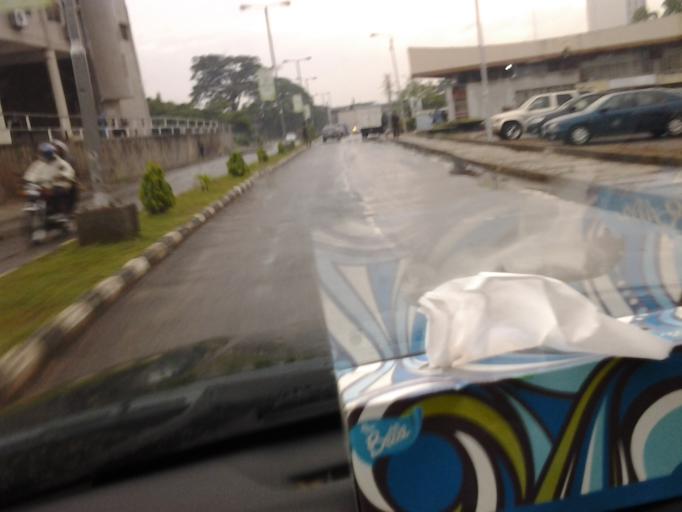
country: NG
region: Oyo
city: Ibadan
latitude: 7.4458
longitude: 3.9008
